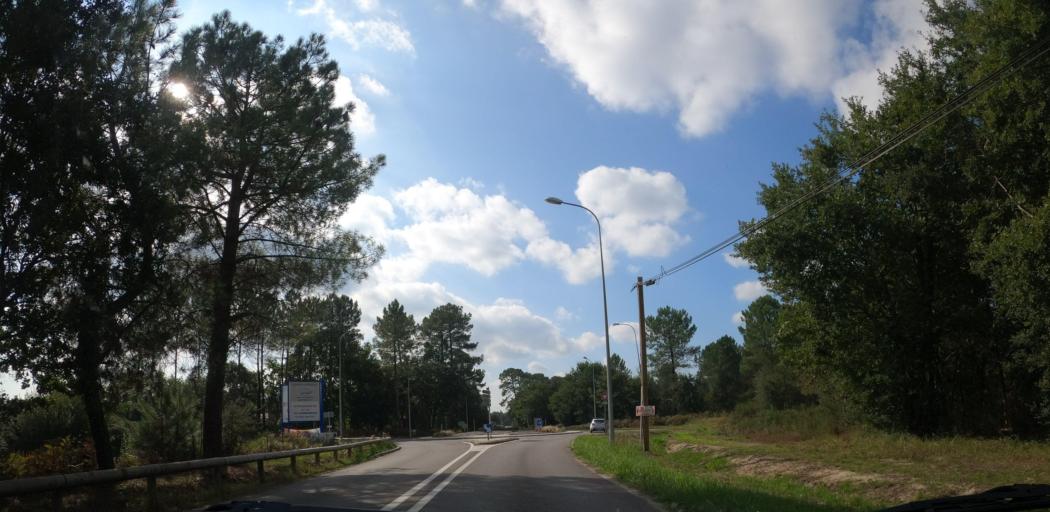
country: FR
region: Aquitaine
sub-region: Departement des Landes
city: Soustons
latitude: 43.7444
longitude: -1.3347
